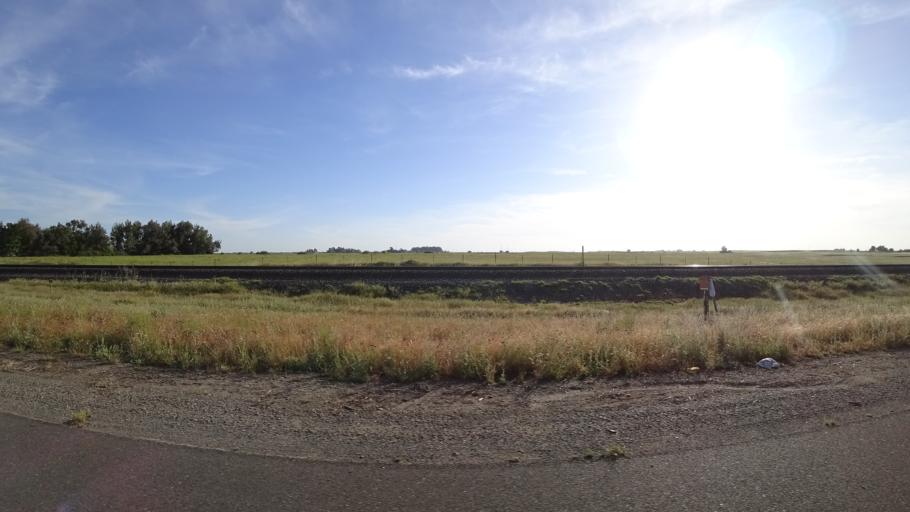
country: US
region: California
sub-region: Placer County
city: Sheridan
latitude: 38.9675
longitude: -121.3652
